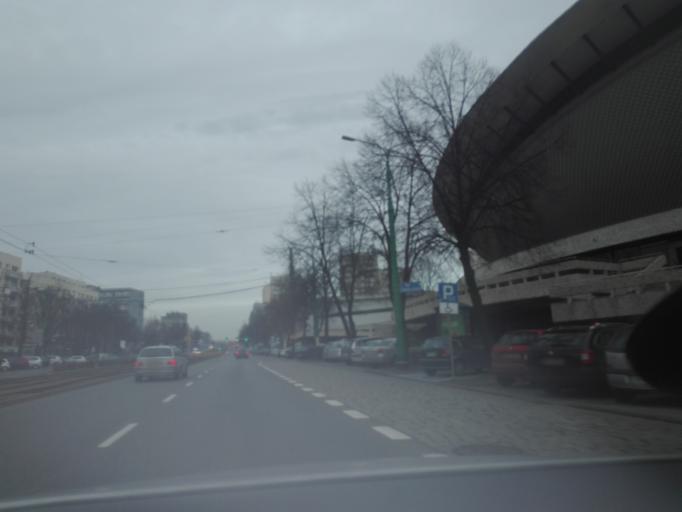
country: PL
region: Silesian Voivodeship
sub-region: Katowice
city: Katowice
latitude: 50.2658
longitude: 19.0241
